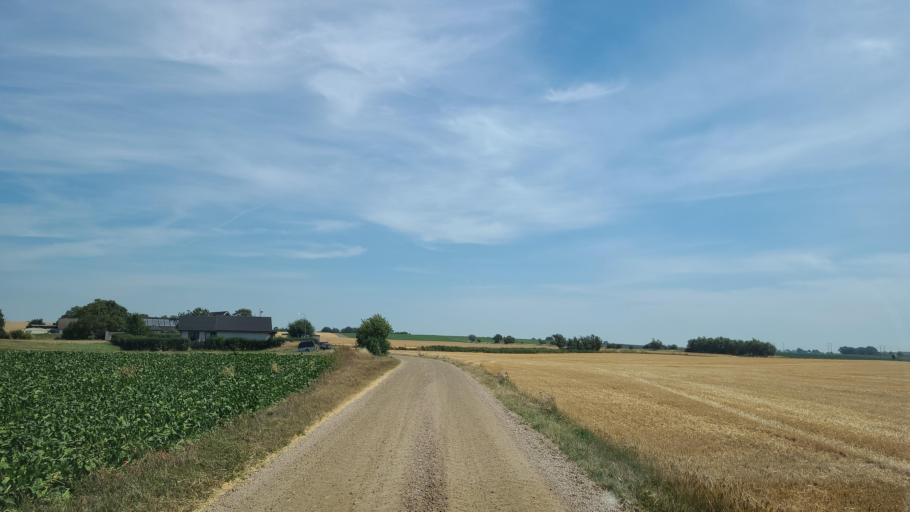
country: SE
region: Skane
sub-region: Trelleborgs Kommun
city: Skare
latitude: 55.4239
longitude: 13.0635
